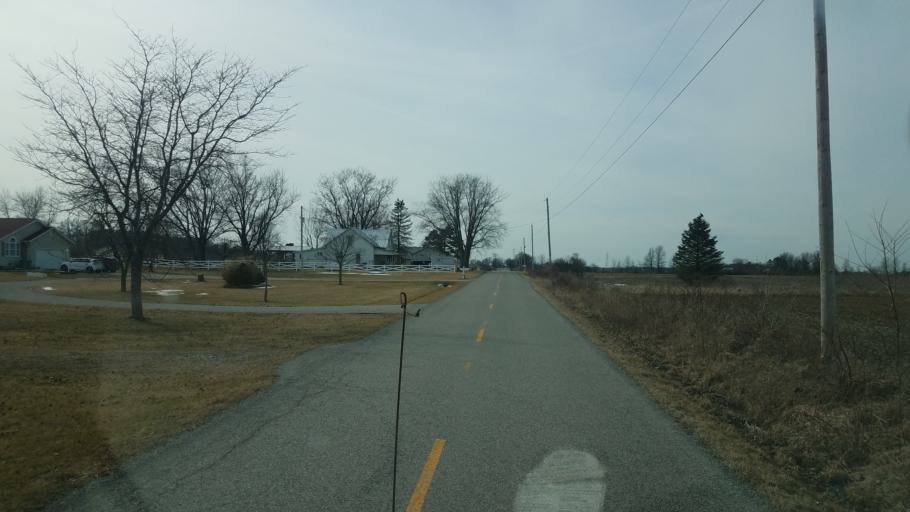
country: US
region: Ohio
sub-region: Union County
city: Richwood
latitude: 40.3164
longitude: -83.2416
